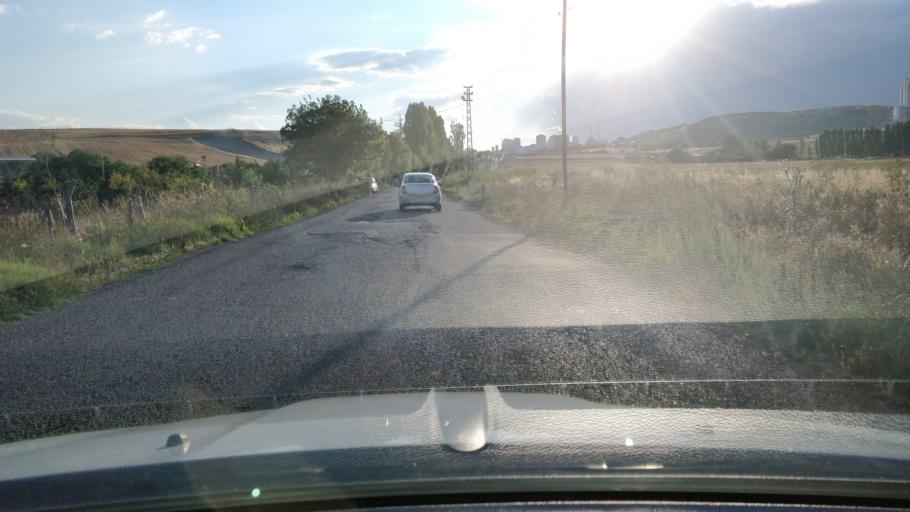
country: TR
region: Ankara
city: Etimesgut
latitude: 39.8258
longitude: 32.5704
